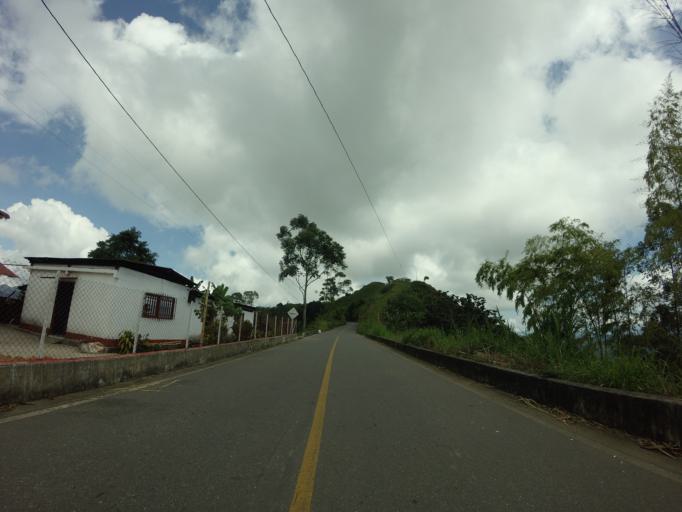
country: CO
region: Caldas
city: Marquetalia
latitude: 5.3017
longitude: -75.0179
